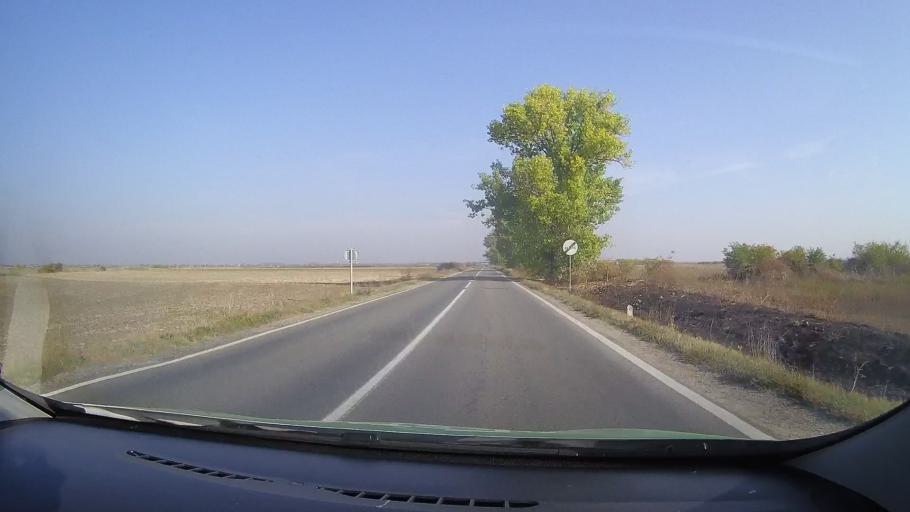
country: RO
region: Arad
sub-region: Comuna Pilu
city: Pilu
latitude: 46.5985
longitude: 21.3494
